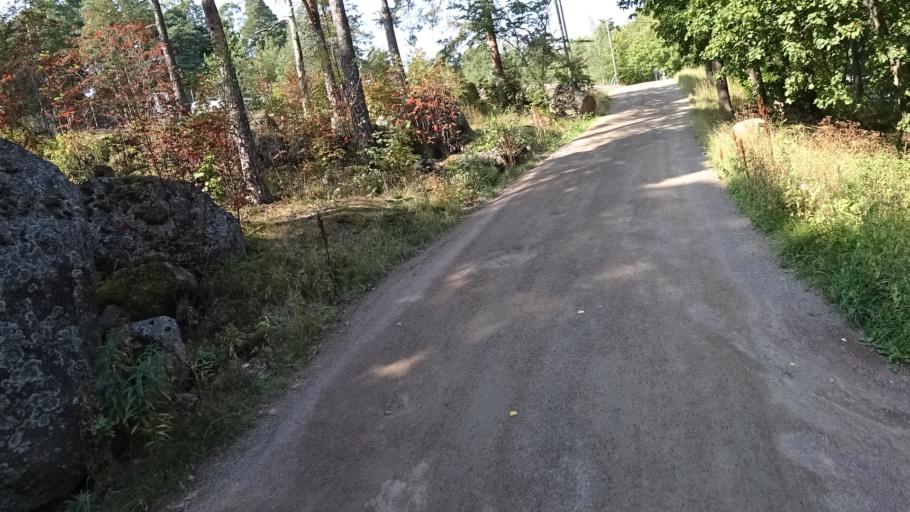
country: FI
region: Kymenlaakso
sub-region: Kotka-Hamina
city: Kotka
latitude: 60.4573
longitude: 26.9501
